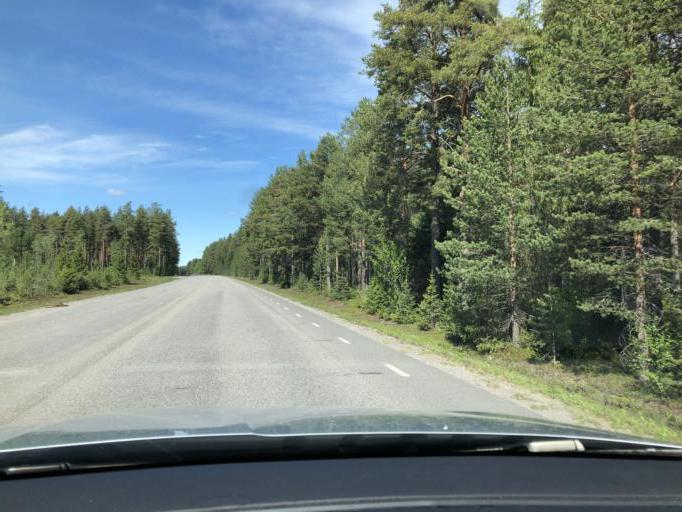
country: SE
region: Norrbotten
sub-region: Pitea Kommun
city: Bergsviken
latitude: 65.3605
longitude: 21.3743
